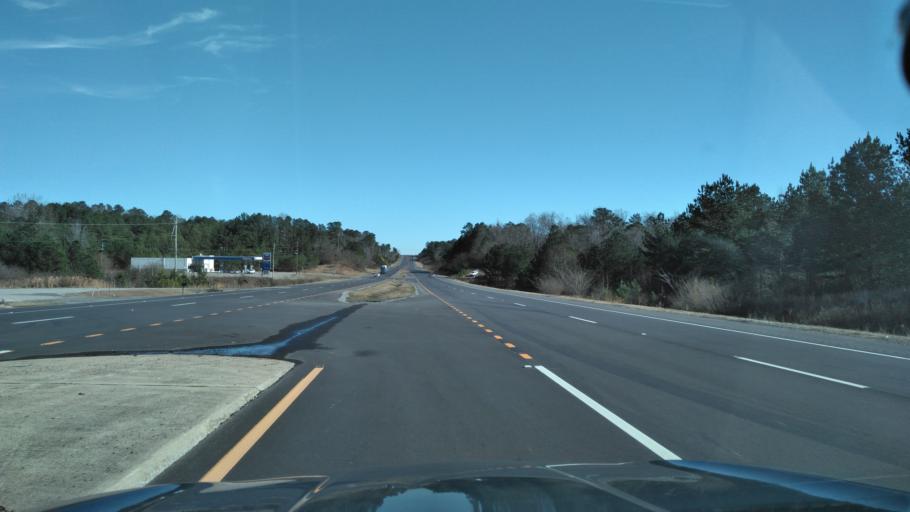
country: US
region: Alabama
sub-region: Walker County
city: Jasper
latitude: 33.8549
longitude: -87.3365
